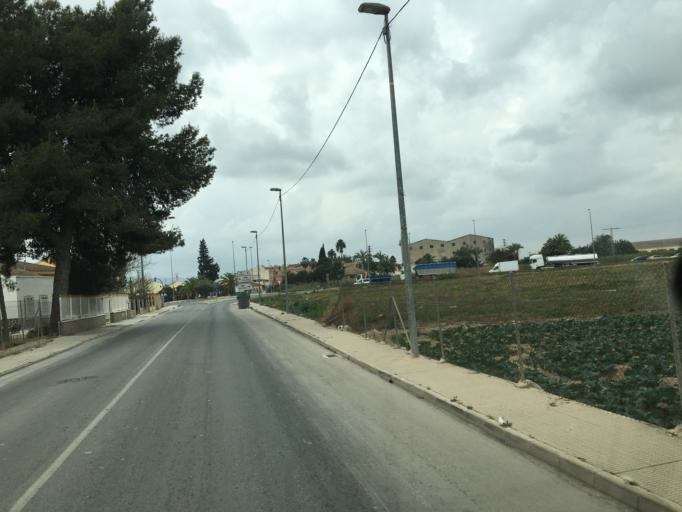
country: ES
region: Murcia
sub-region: Murcia
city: Beniel
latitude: 38.0226
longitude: -1.0325
